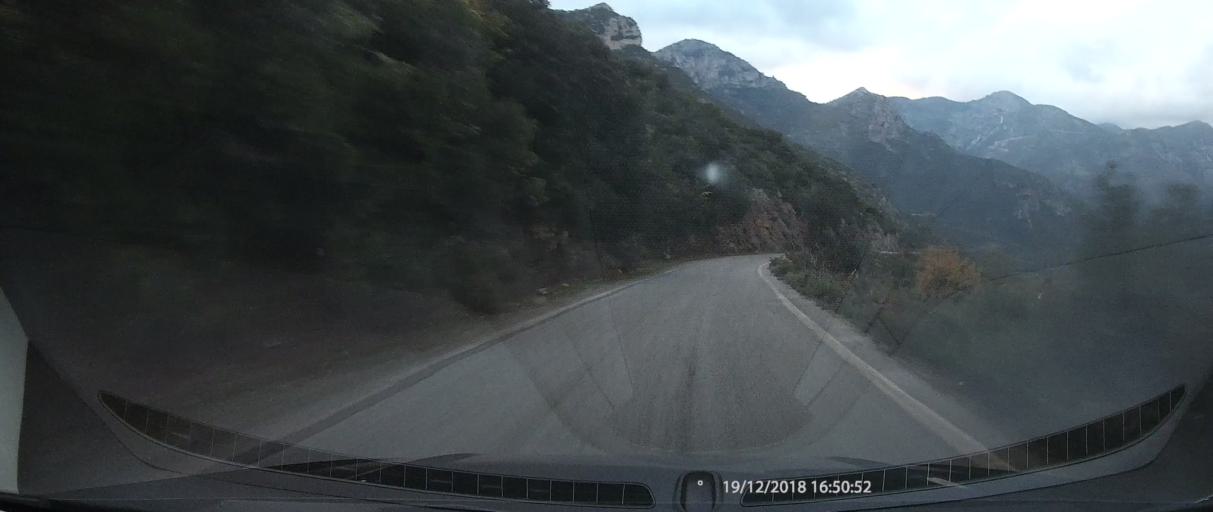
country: GR
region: Peloponnese
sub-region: Nomos Lakonias
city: Sykea
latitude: 36.9524
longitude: 22.9938
